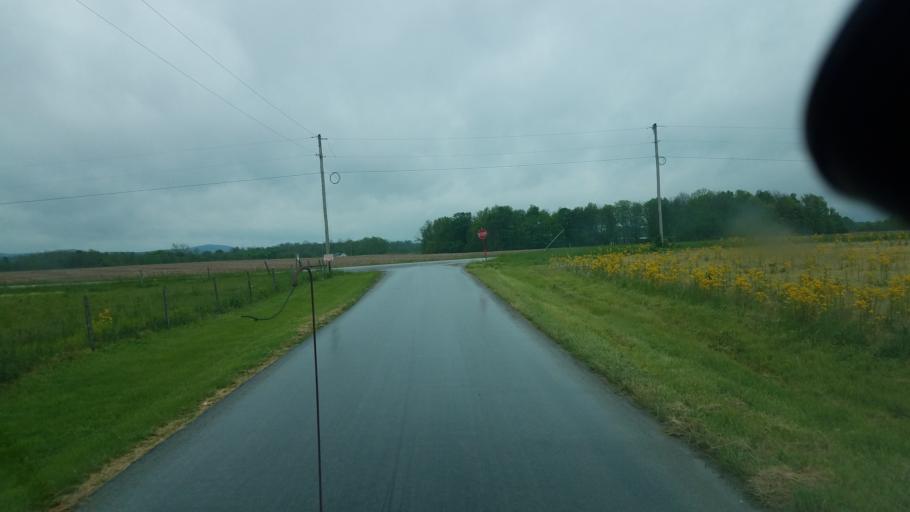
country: US
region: Ohio
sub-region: Highland County
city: Greenfield
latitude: 39.3211
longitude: -83.4212
